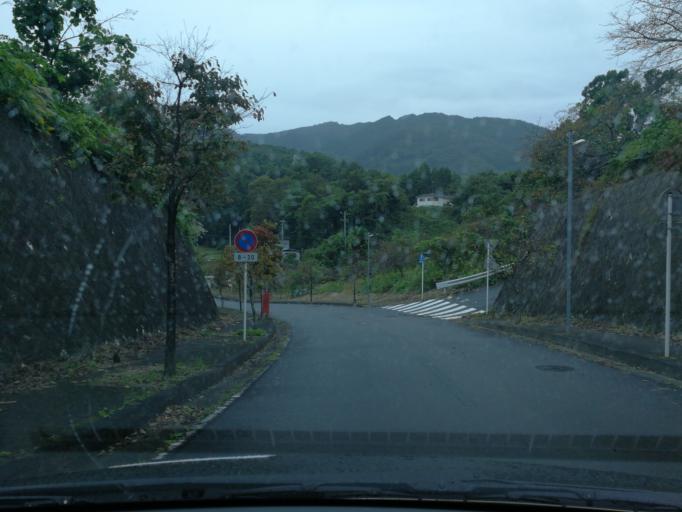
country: JP
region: Yamanashi
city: Uenohara
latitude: 35.6008
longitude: 139.2109
